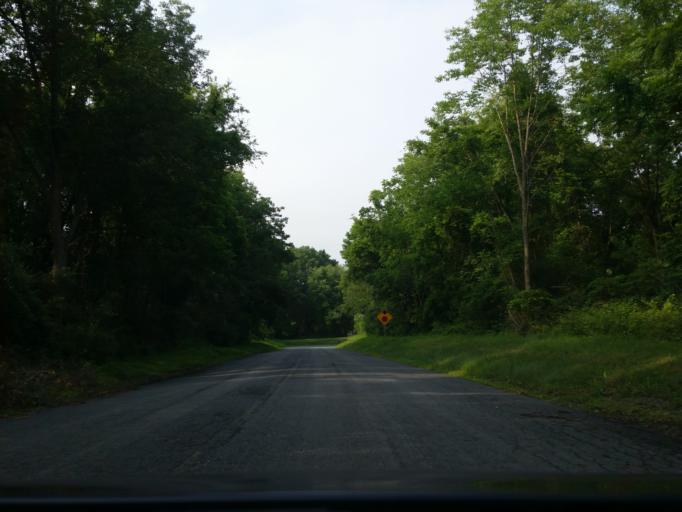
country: US
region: Pennsylvania
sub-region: Lebanon County
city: Jonestown
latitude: 40.4173
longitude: -76.5800
